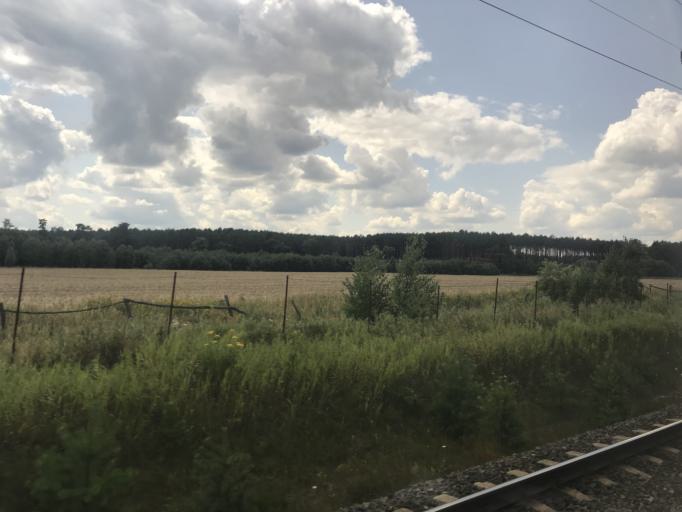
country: PL
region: Lubusz
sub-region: Powiat sulecinski
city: Torzym
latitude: 52.3190
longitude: 15.0250
